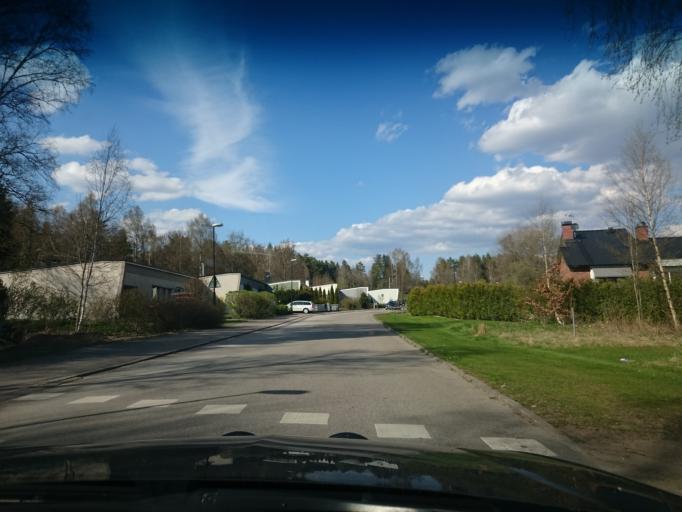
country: SE
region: Joenkoeping
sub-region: Vetlanda Kommun
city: Vetlanda
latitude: 57.4266
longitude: 15.0980
